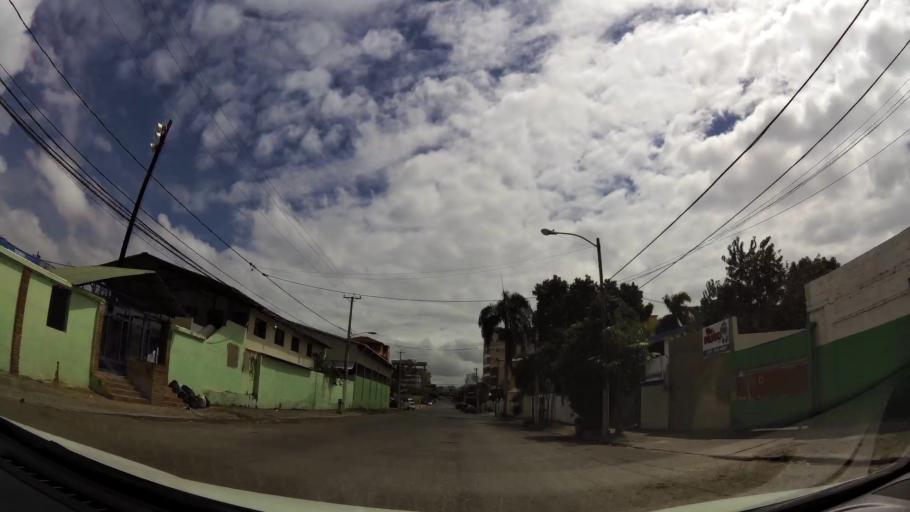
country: DO
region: Nacional
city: Bella Vista
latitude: 18.4718
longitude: -69.9570
